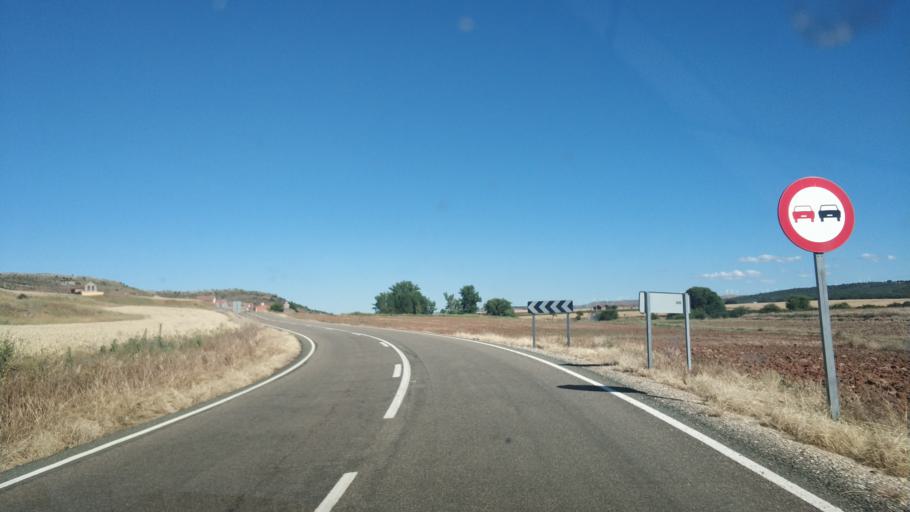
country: ES
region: Castille and Leon
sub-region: Provincia de Soria
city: Montejo de Tiermes
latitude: 41.3633
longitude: -3.1877
